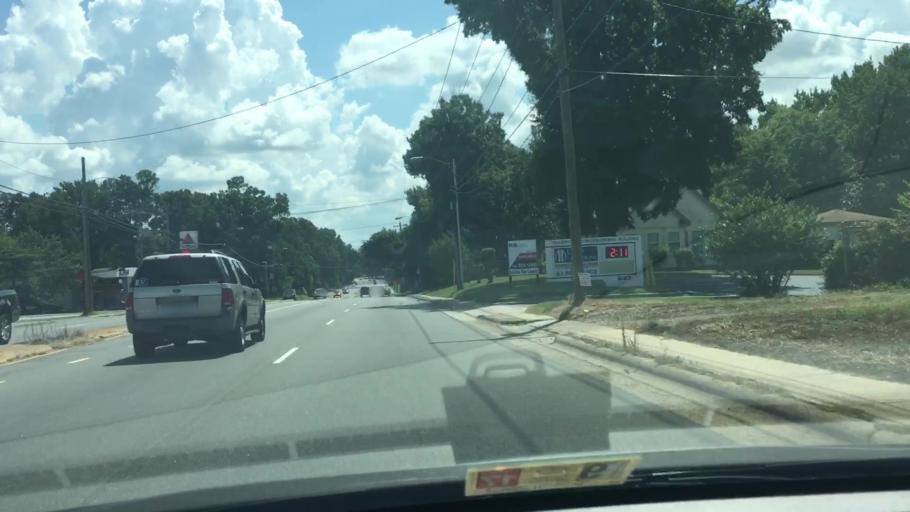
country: US
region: North Carolina
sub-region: Mecklenburg County
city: Charlotte
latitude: 35.2665
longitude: -80.7950
